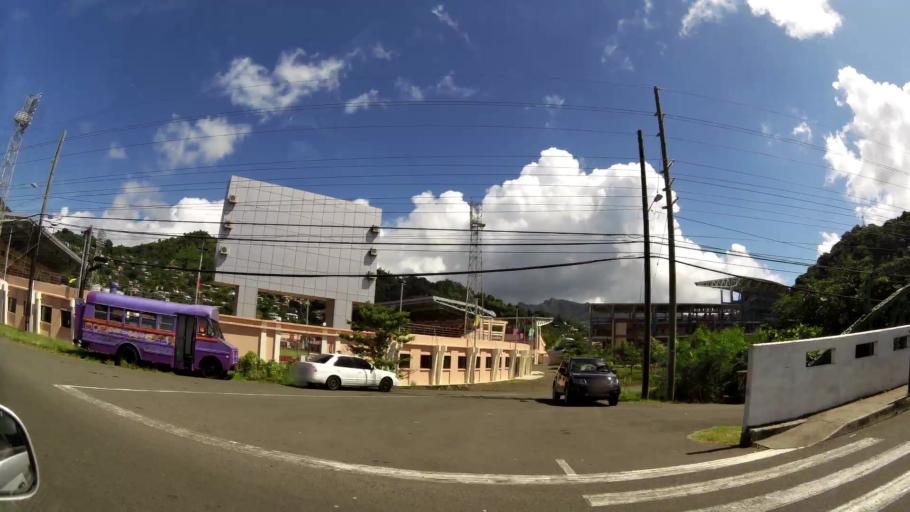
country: GD
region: Saint George
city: Saint George's
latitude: 12.0590
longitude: -61.7545
